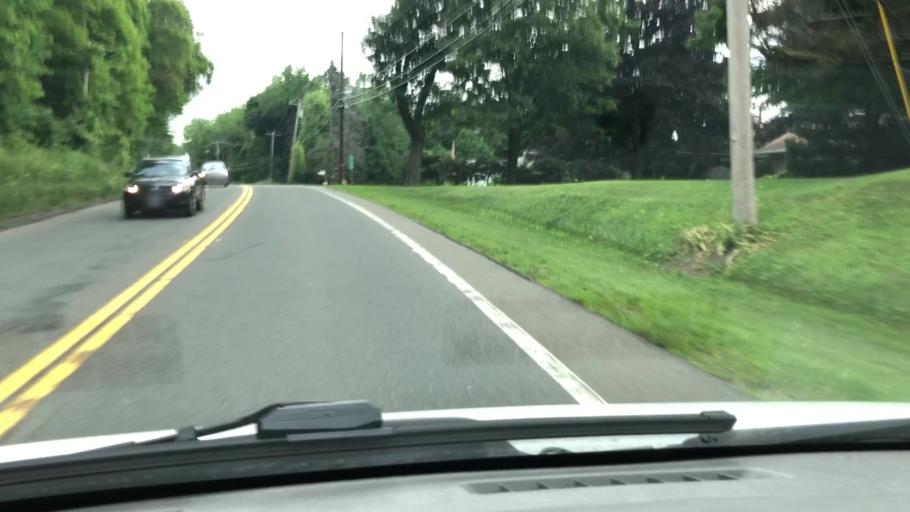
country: US
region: Massachusetts
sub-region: Berkshire County
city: Adams
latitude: 42.5791
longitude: -73.1492
